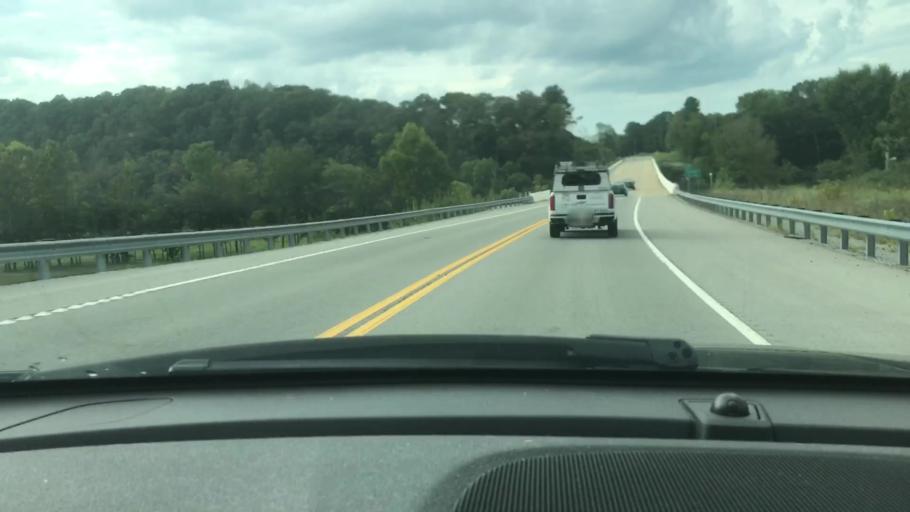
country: US
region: Tennessee
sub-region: Cheatham County
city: Ashland City
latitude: 36.2825
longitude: -87.1453
